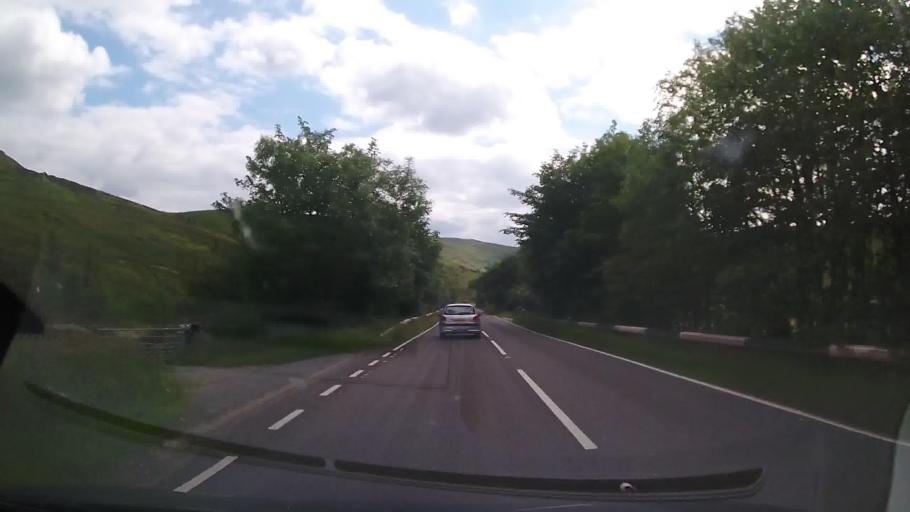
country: GB
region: Wales
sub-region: Gwynedd
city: Trawsfynydd
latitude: 52.9277
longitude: -3.8200
